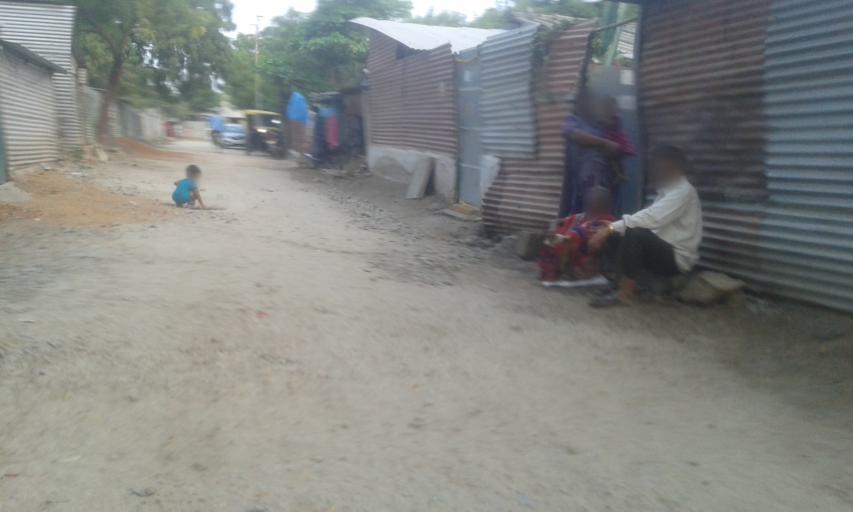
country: IN
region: Karnataka
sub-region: Raichur
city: Lingsugur
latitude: 16.1952
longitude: 76.6633
